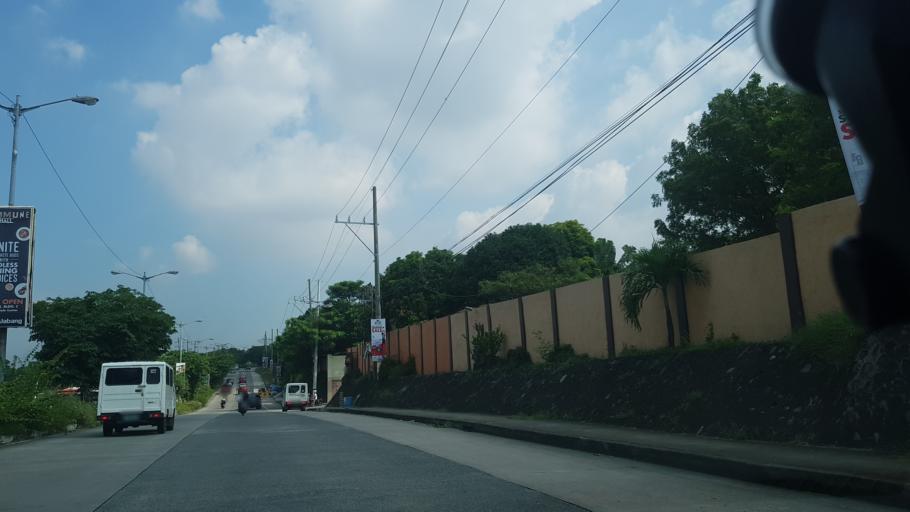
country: PH
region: Calabarzon
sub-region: Province of Laguna
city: San Pedro
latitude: 14.3886
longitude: 121.0098
